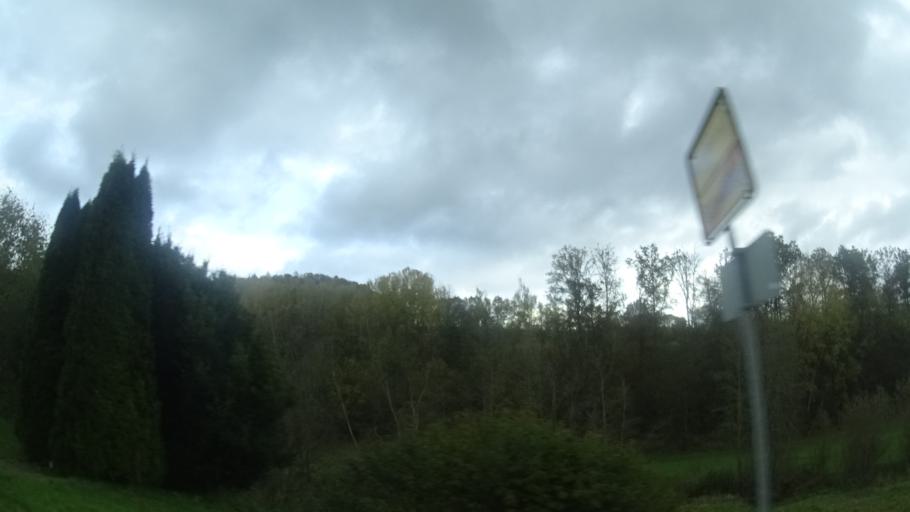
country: DE
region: Bavaria
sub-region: Regierungsbezirk Unterfranken
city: Hohenroth
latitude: 50.3548
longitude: 10.1160
